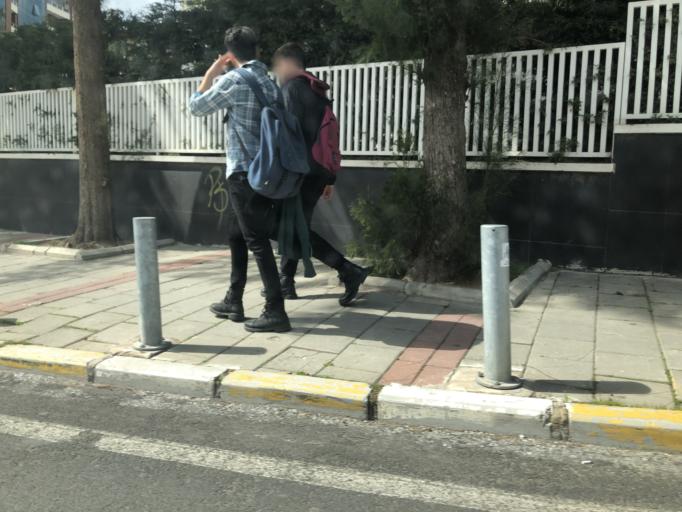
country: TR
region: Izmir
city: Karabaglar
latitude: 38.3902
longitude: 27.0448
